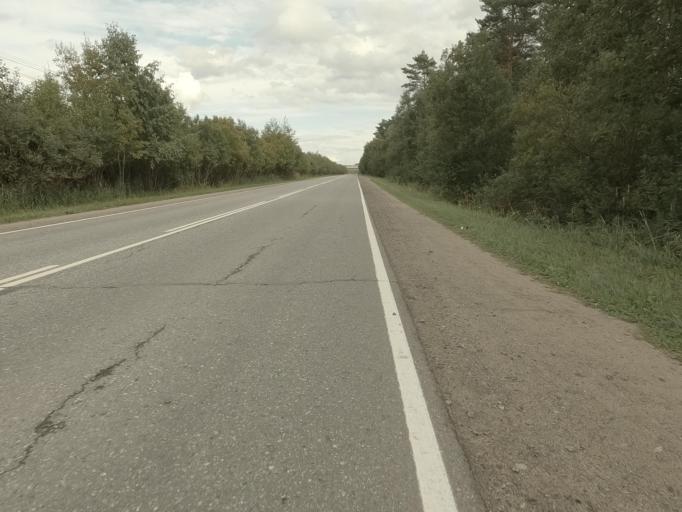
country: RU
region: Leningrad
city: Mga
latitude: 59.7612
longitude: 31.0049
